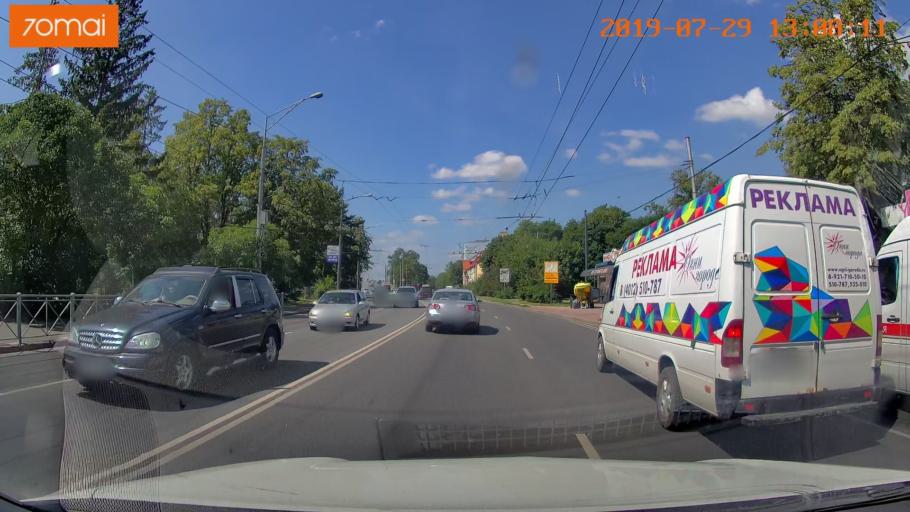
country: RU
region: Kaliningrad
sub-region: Gorod Kaliningrad
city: Kaliningrad
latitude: 54.7117
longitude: 20.4362
